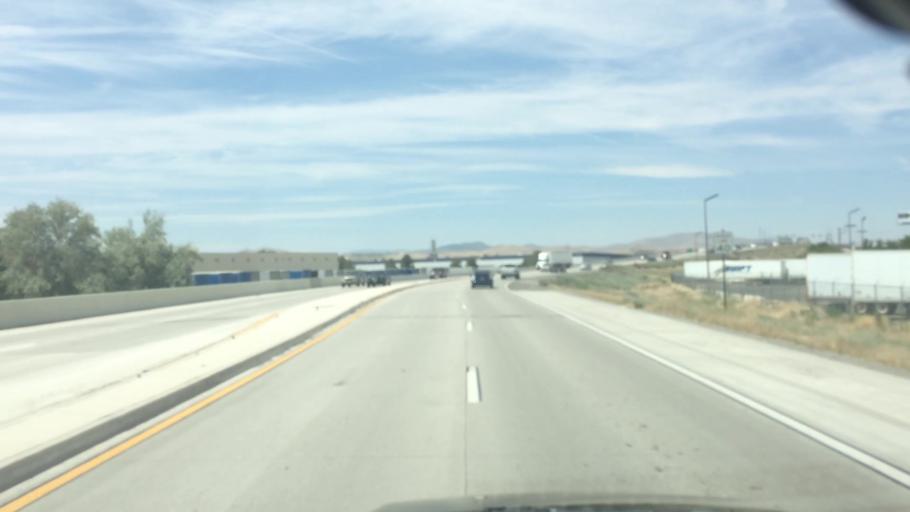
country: US
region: Nevada
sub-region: Washoe County
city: Sparks
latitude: 39.5234
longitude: -119.7138
